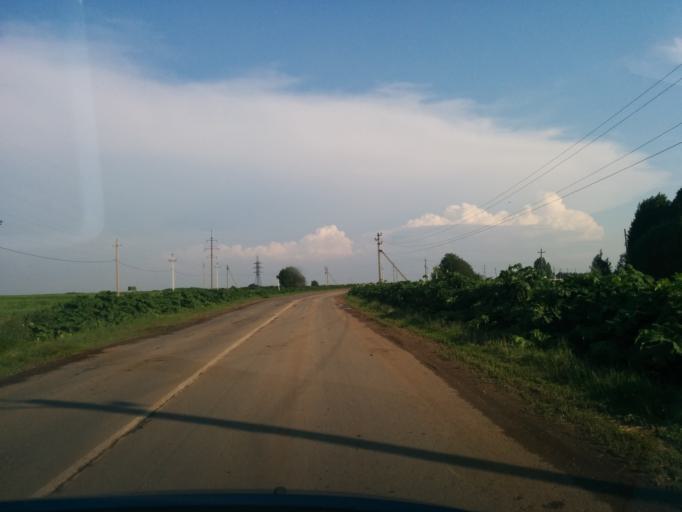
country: RU
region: Perm
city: Polazna
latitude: 58.2238
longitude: 56.2962
